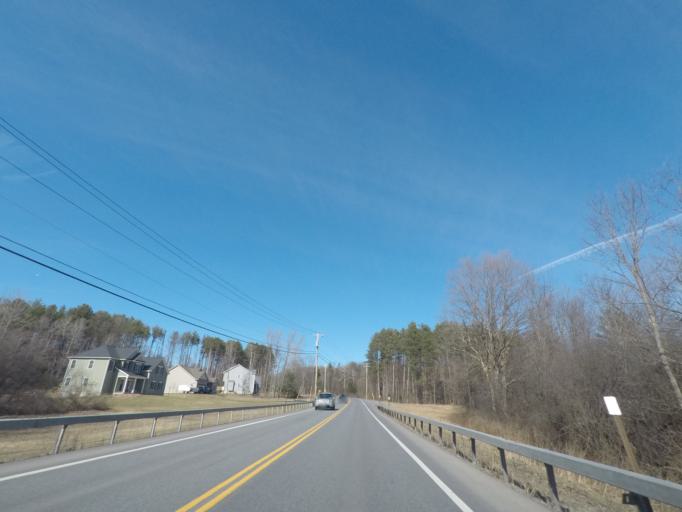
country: US
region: New York
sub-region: Saratoga County
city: Milton
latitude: 43.0674
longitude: -73.8492
